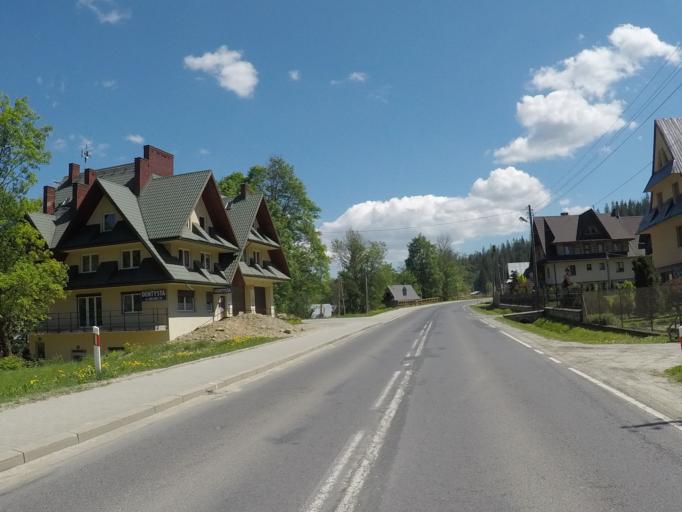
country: PL
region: Lesser Poland Voivodeship
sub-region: Powiat tatrzanski
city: Bukowina Tatrzanska
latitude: 49.3355
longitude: 20.0666
